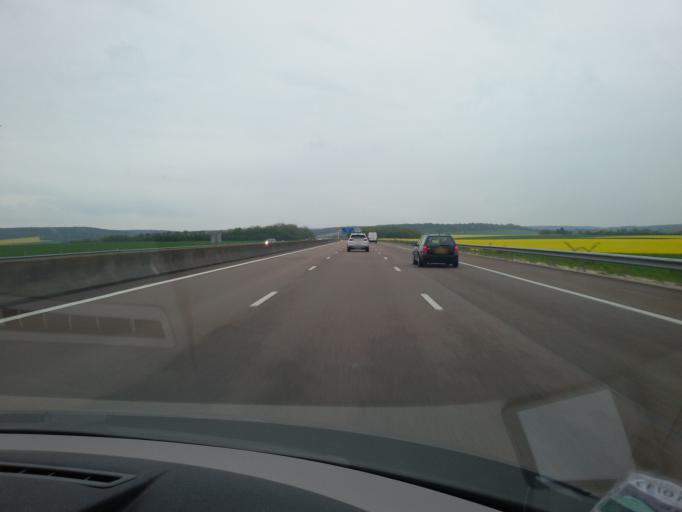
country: FR
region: Bourgogne
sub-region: Departement de la Cote-d'Or
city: Selongey
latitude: 47.5322
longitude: 5.1993
